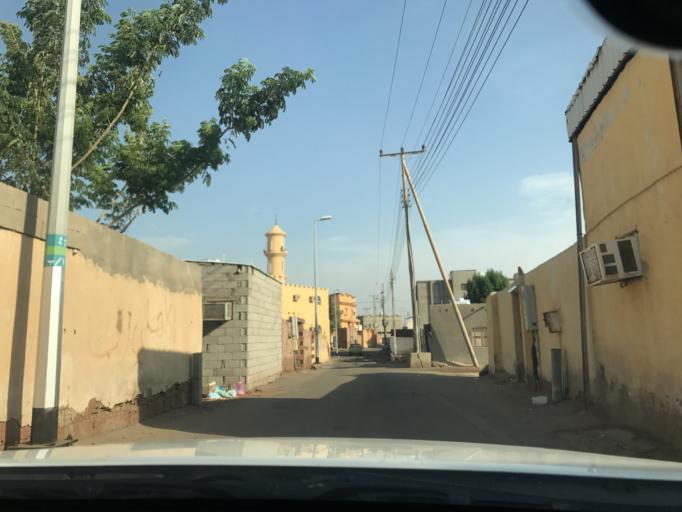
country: SA
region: Makkah
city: Al Jumum
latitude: 21.4454
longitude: 39.5339
